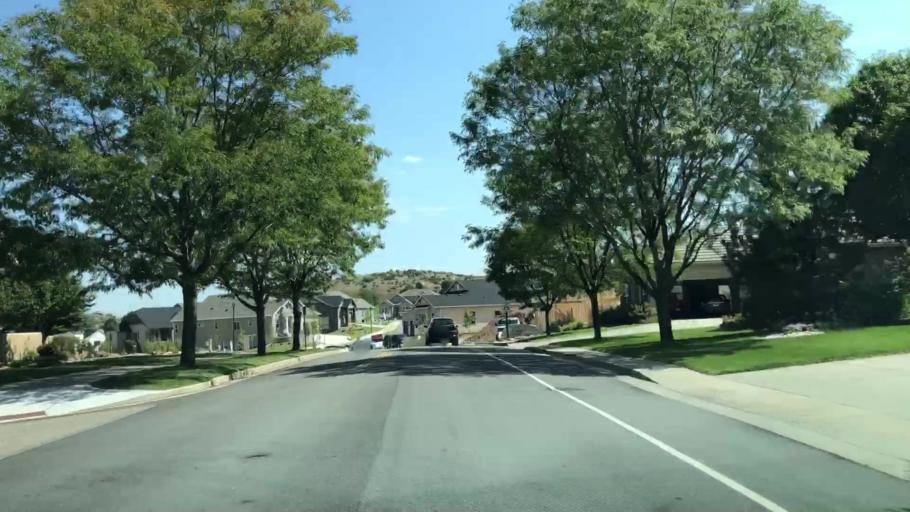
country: US
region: Colorado
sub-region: Larimer County
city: Loveland
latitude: 40.4014
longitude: -105.1448
